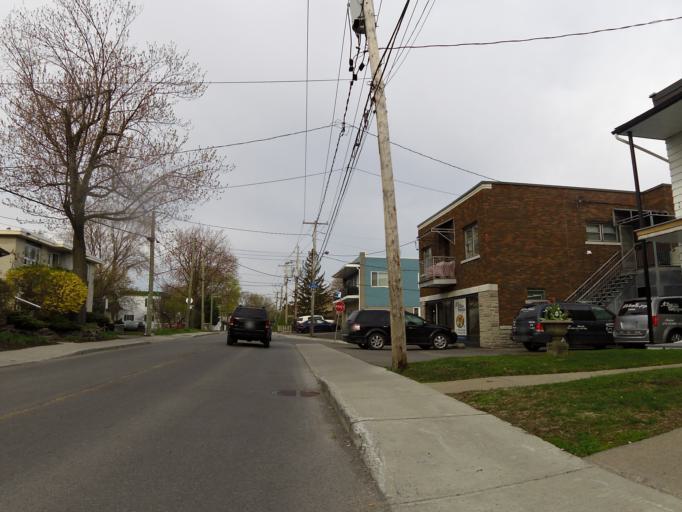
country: CA
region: Quebec
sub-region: Laval
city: Laval
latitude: 45.5491
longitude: -73.7025
